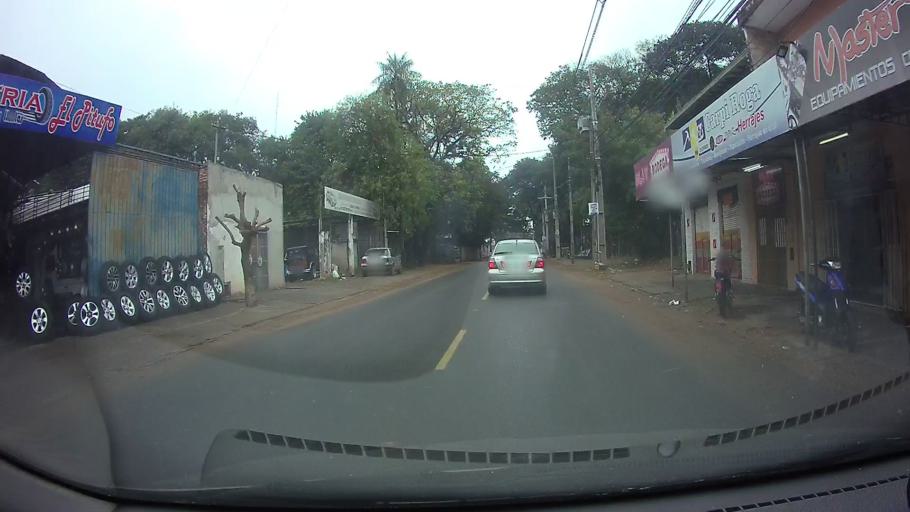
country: PY
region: Central
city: Villa Elisa
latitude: -25.3454
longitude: -57.5695
